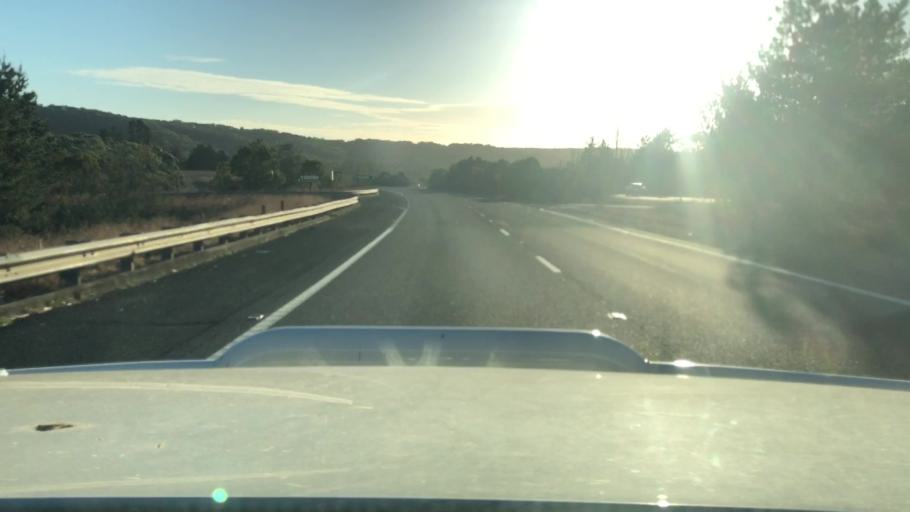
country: AU
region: New South Wales
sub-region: Wingecarribee
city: Bundanoon
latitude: -34.6482
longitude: 150.1176
